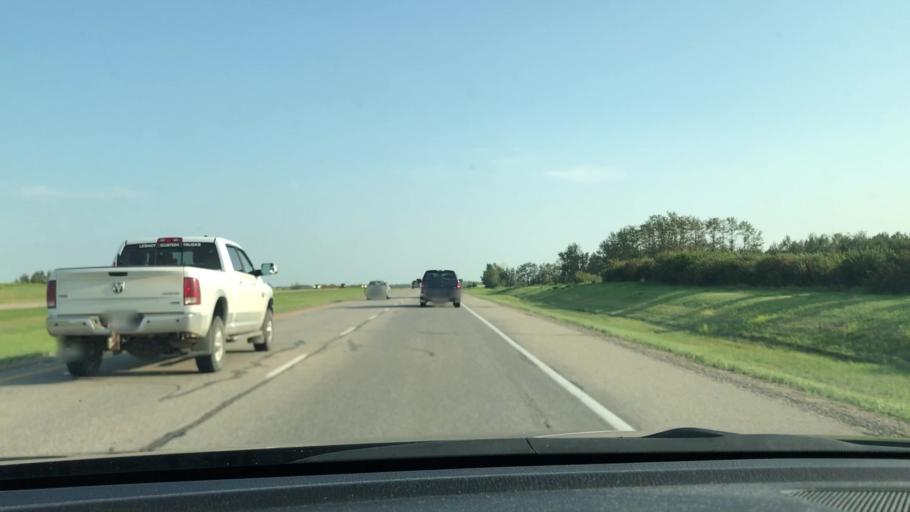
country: CA
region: Alberta
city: Millet
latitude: 53.0725
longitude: -113.5985
